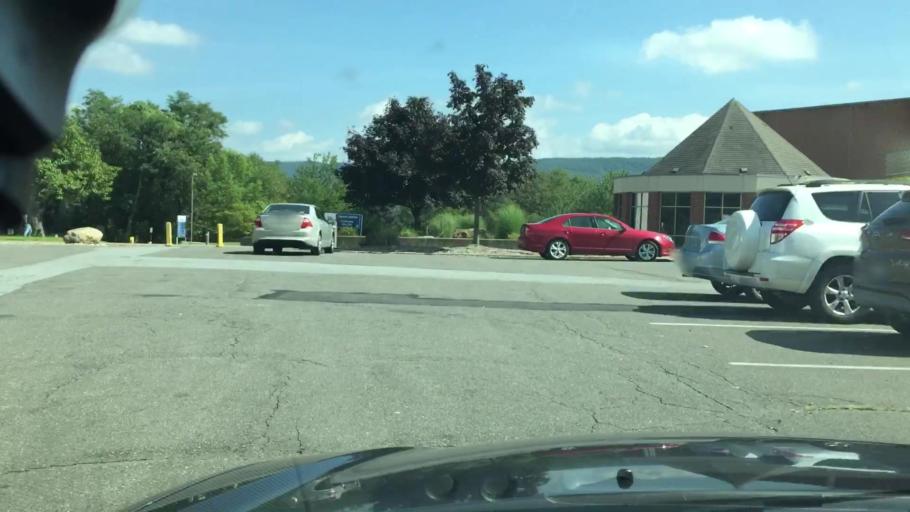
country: US
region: Pennsylvania
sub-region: Luzerne County
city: Nanticoke
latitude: 41.1940
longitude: -75.9936
